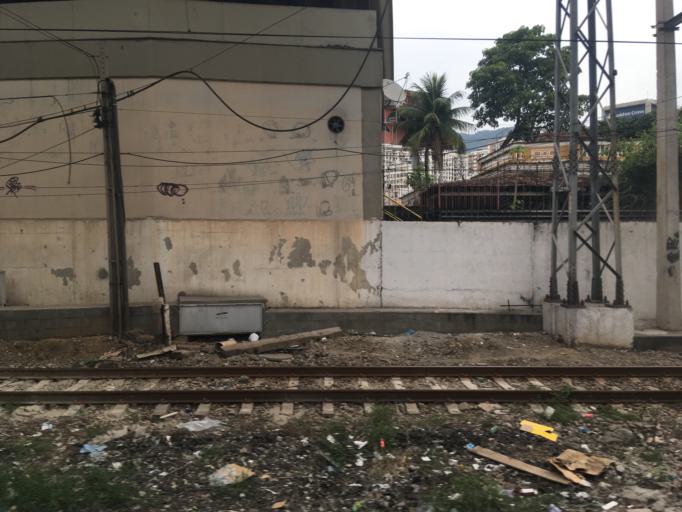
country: BR
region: Rio de Janeiro
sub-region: Rio De Janeiro
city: Rio de Janeiro
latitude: -22.9098
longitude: -43.2223
